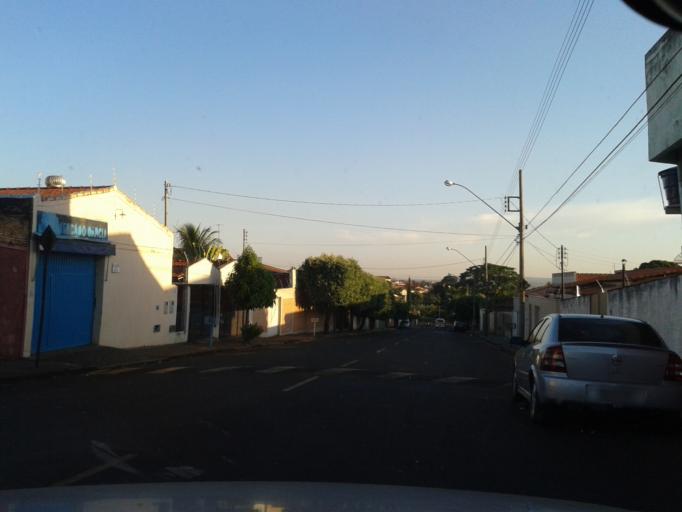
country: BR
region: Minas Gerais
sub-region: Ituiutaba
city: Ituiutaba
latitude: -18.9786
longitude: -49.4688
